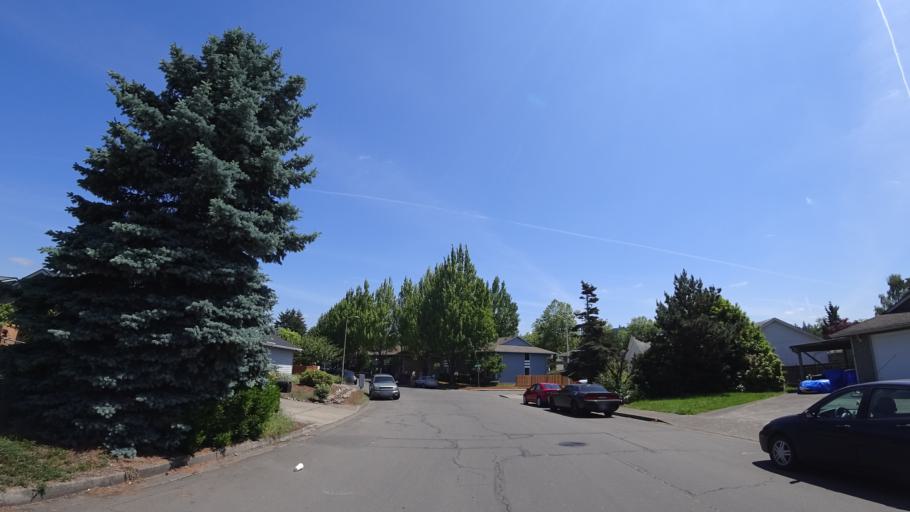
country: US
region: Oregon
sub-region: Multnomah County
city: Gresham
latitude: 45.4910
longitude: -122.4905
